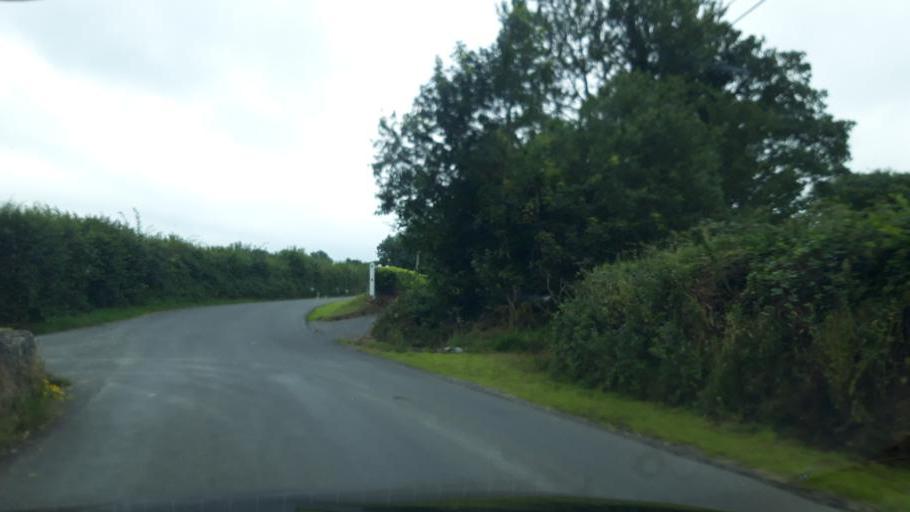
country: IE
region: Leinster
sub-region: Kilkenny
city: Ballyragget
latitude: 52.7141
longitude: -7.4026
